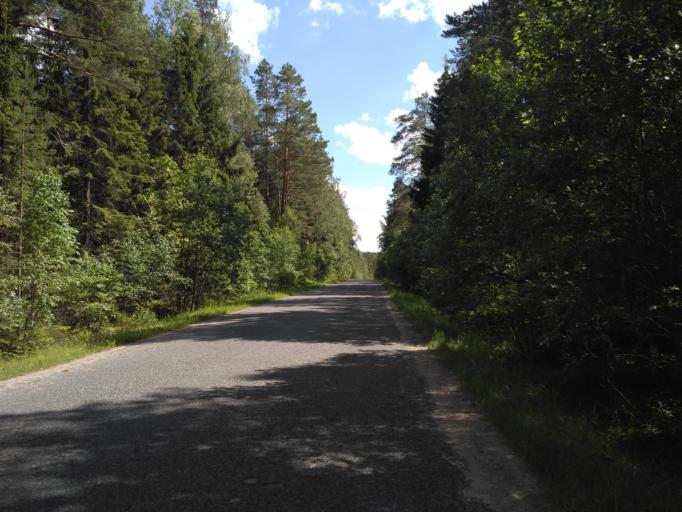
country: BY
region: Minsk
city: Horad Barysaw
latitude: 54.0305
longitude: 28.6337
